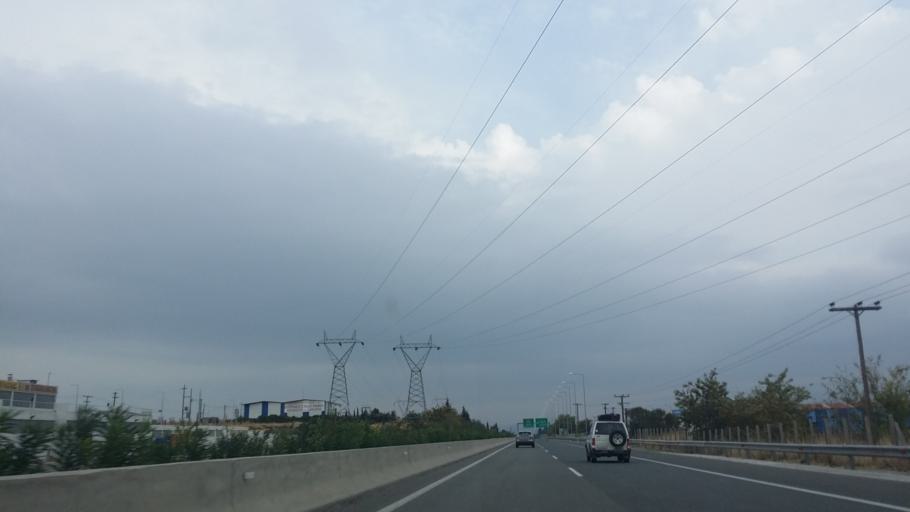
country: GR
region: Central Greece
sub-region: Nomos Voiotias
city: Schimatari
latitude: 38.3585
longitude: 23.5607
